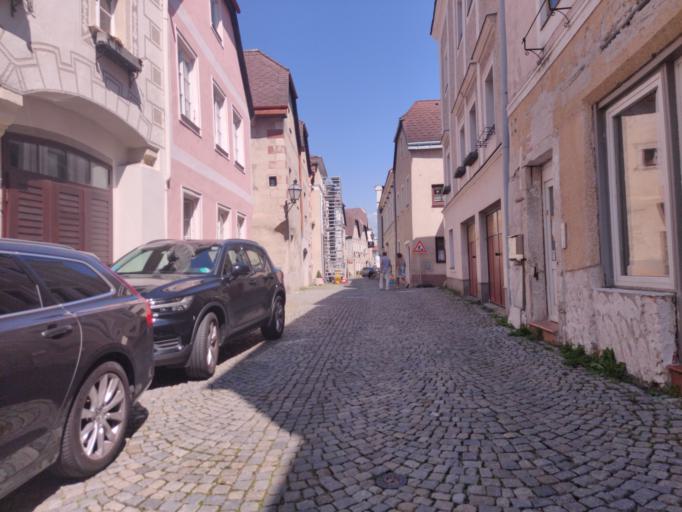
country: AT
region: Lower Austria
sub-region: Politischer Bezirk Krems
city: Weinzierl bei Krems
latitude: 48.4027
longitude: 15.5840
